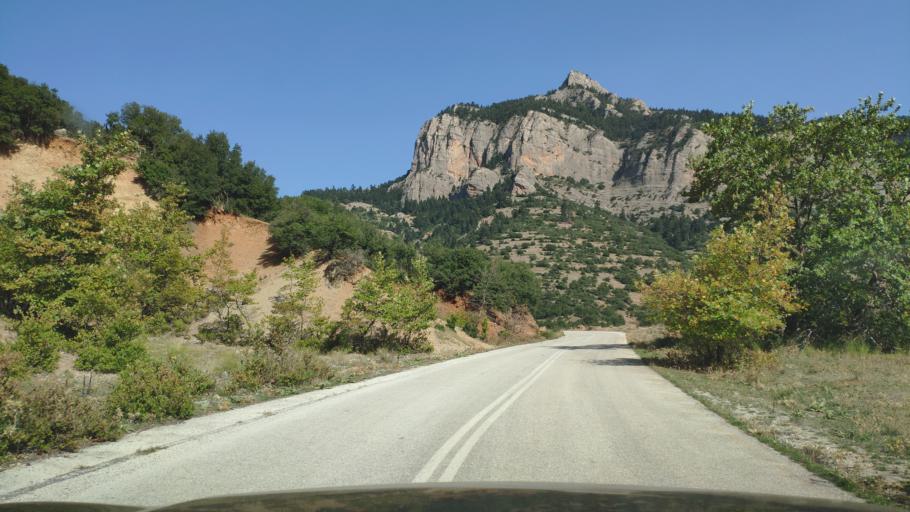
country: GR
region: West Greece
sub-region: Nomos Achaias
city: Aiyira
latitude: 37.9708
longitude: 22.3500
